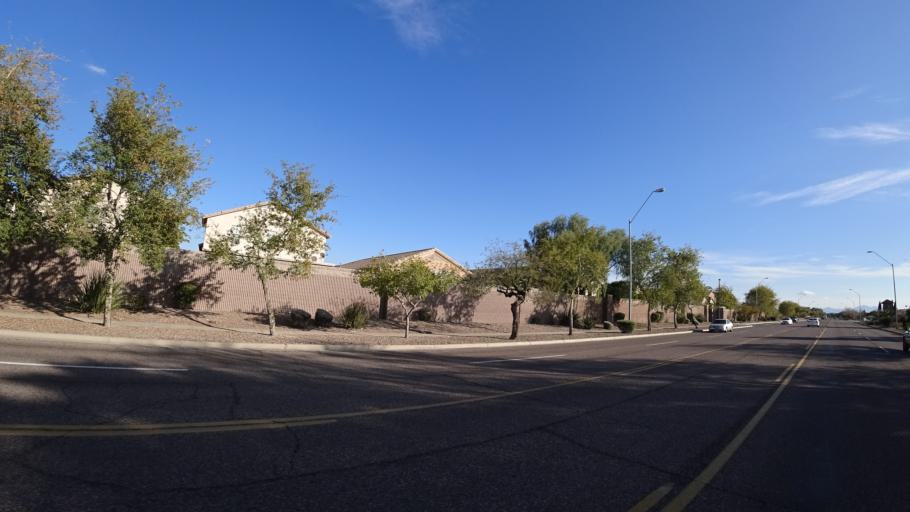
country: US
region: Arizona
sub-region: Maricopa County
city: Sun City
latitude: 33.6504
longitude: -112.2551
